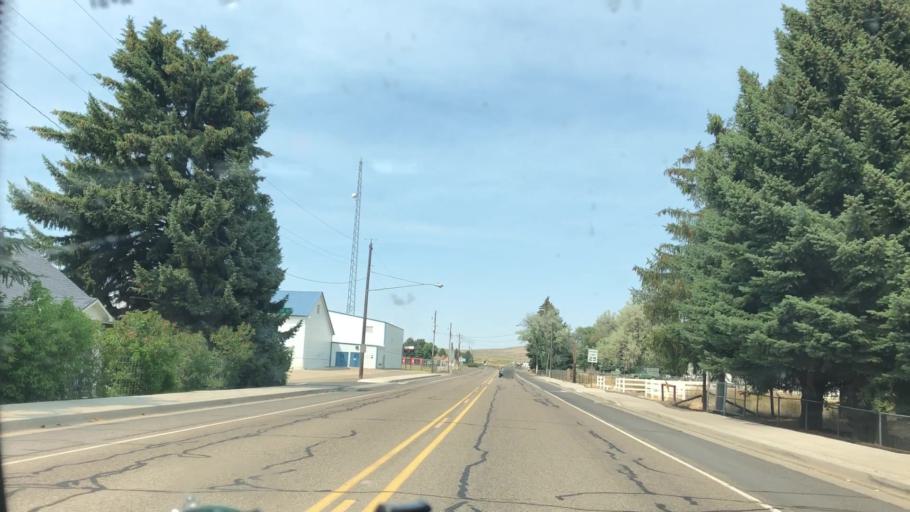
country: US
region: Idaho
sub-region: Owyhee County
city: Murphy
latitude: 42.9768
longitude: -117.0531
